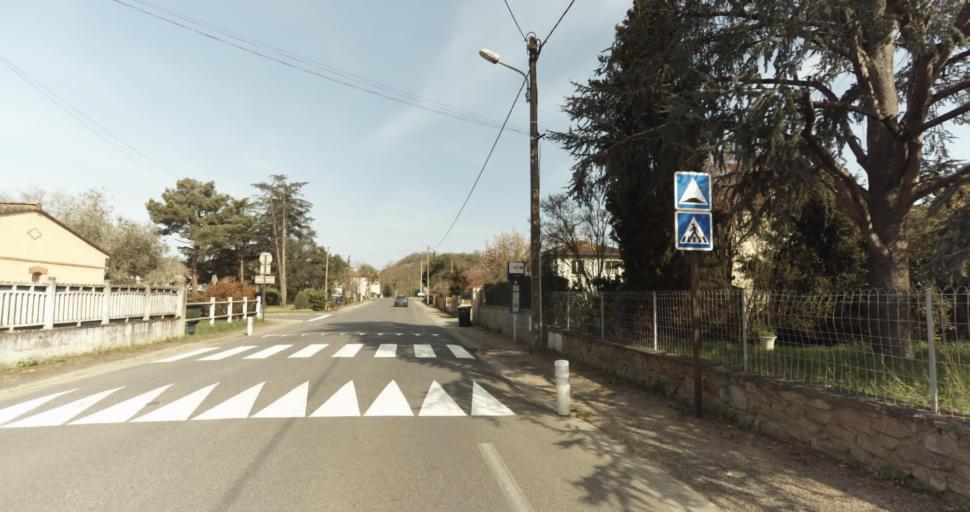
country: FR
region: Midi-Pyrenees
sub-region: Departement du Tarn
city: Saint-Sulpice-la-Pointe
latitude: 43.7822
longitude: 1.6799
